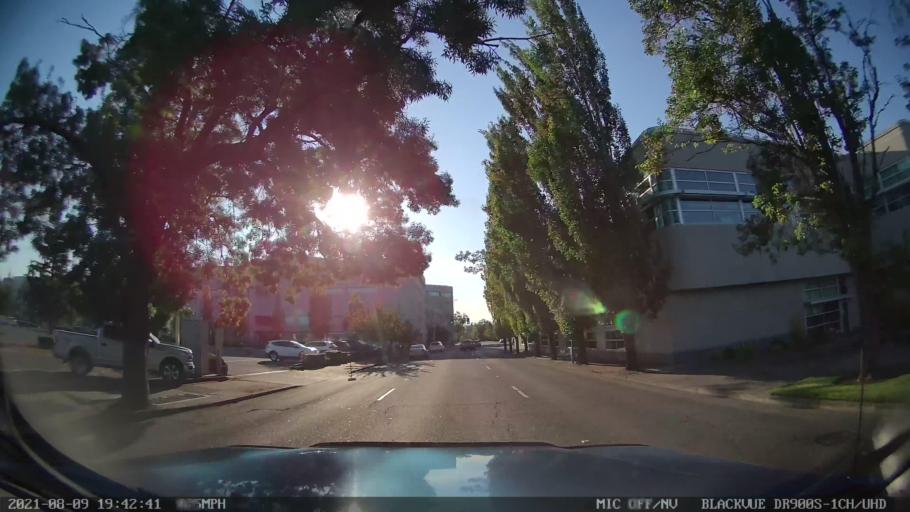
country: US
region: Oregon
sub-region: Marion County
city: Salem
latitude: 44.9415
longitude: -123.0260
